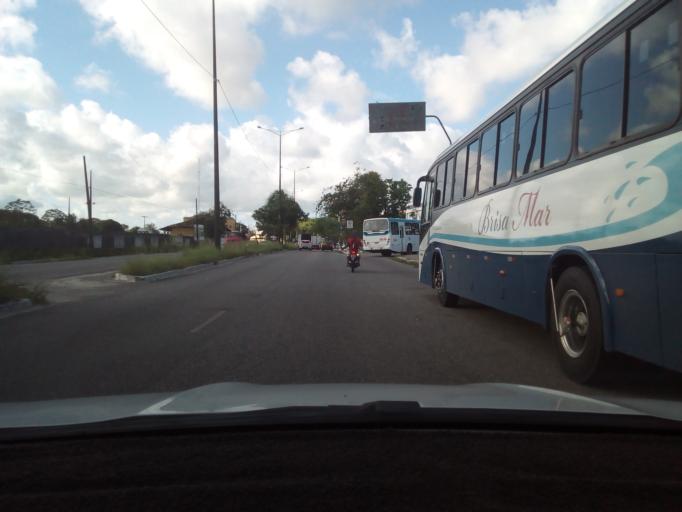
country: BR
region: Paraiba
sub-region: Joao Pessoa
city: Joao Pessoa
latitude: -7.1170
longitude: -34.8913
